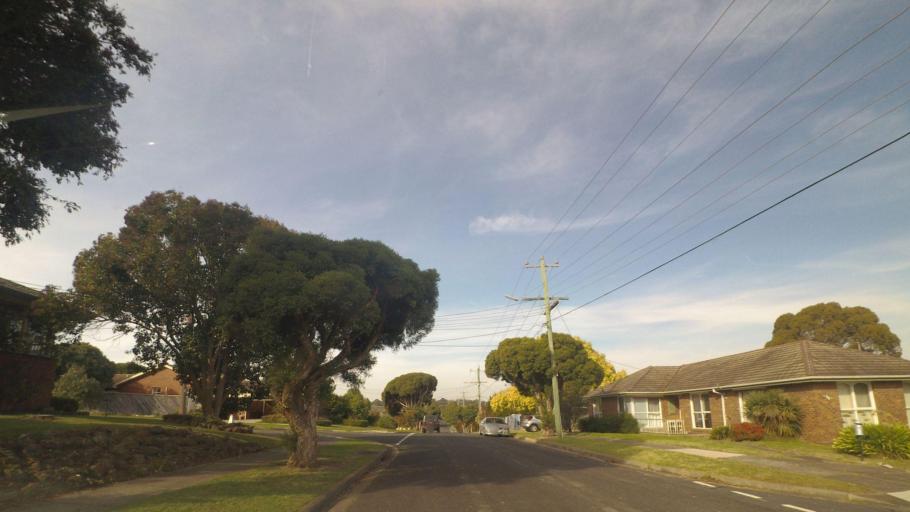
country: AU
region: Victoria
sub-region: Manningham
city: Doncaster East
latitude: -37.7768
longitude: 145.1504
